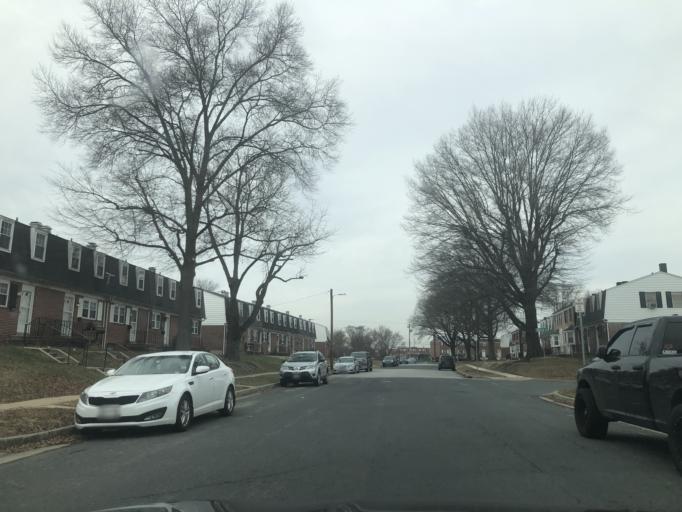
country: US
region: Maryland
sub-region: Baltimore County
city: Dundalk
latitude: 39.2617
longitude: -76.4957
